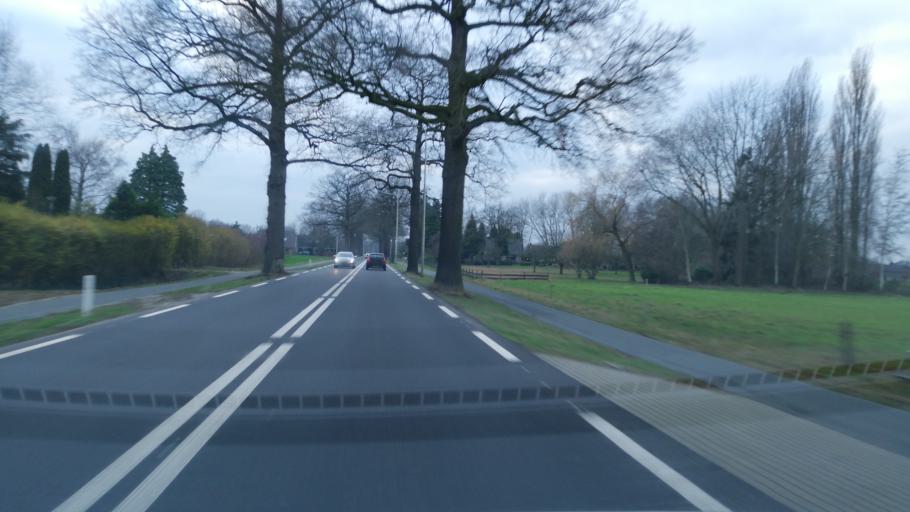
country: NL
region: Gelderland
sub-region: Gemeente Apeldoorn
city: Apeldoorn
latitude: 52.2316
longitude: 6.0300
